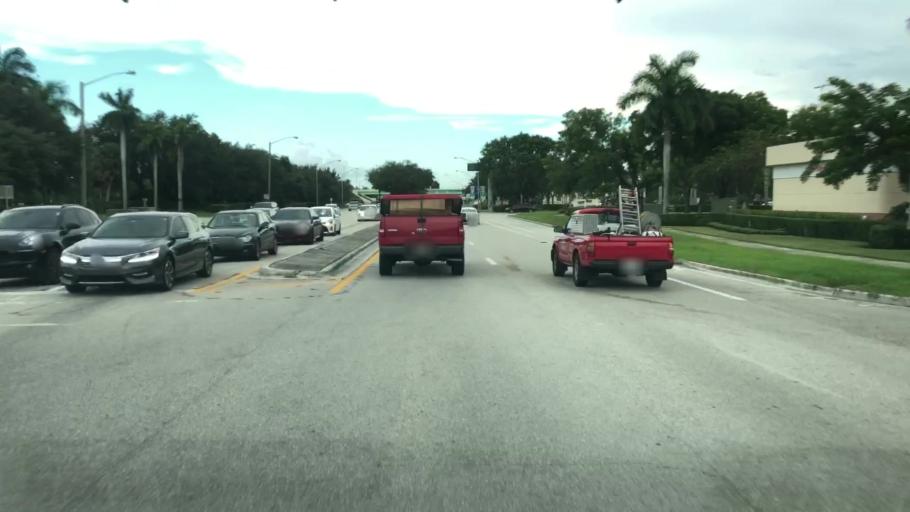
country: US
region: Florida
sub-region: Broward County
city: Coral Springs
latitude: 26.3063
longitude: -80.2789
